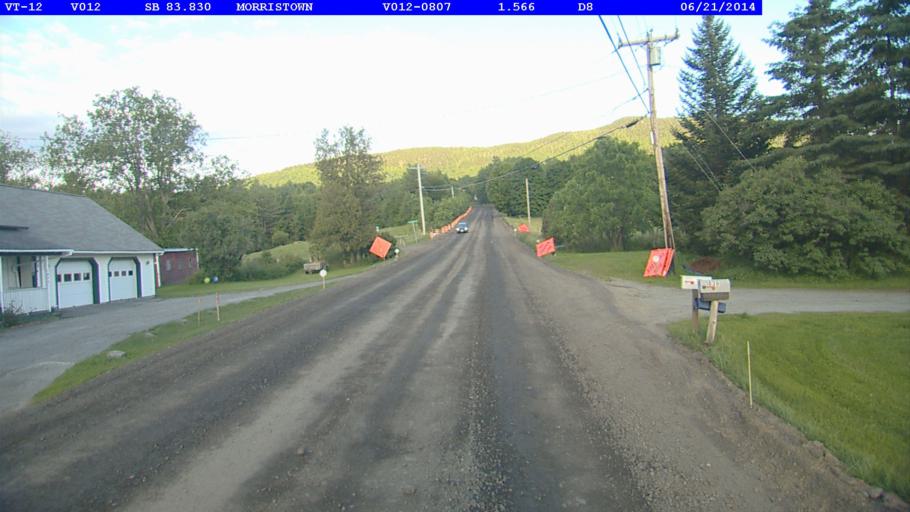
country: US
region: Vermont
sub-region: Lamoille County
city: Morrisville
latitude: 44.5491
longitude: -72.5679
